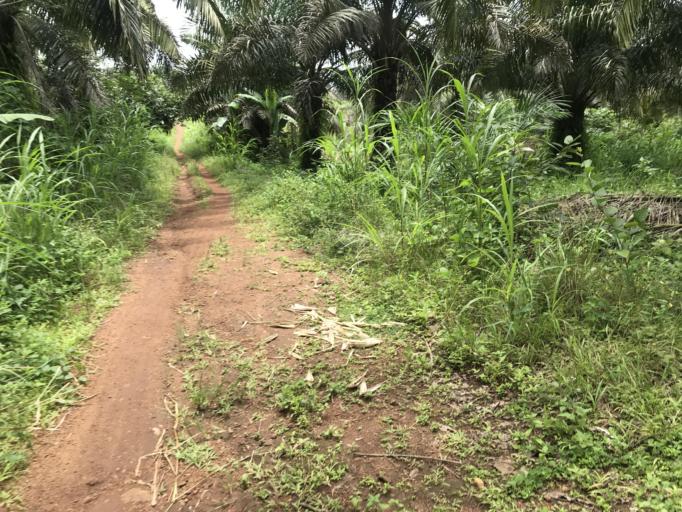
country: GN
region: Nzerekore
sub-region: Prefecture de Guekedou
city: Gueckedou
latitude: 8.4978
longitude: -10.3246
